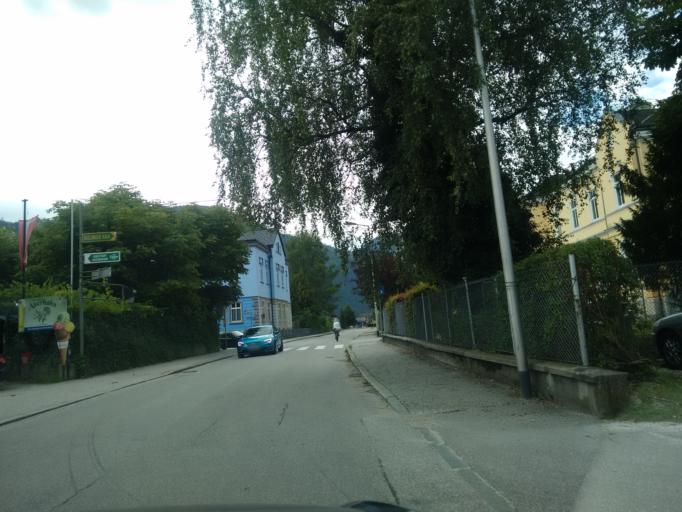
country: AT
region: Upper Austria
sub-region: Politischer Bezirk Gmunden
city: Ebensee
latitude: 47.8052
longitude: 13.7709
